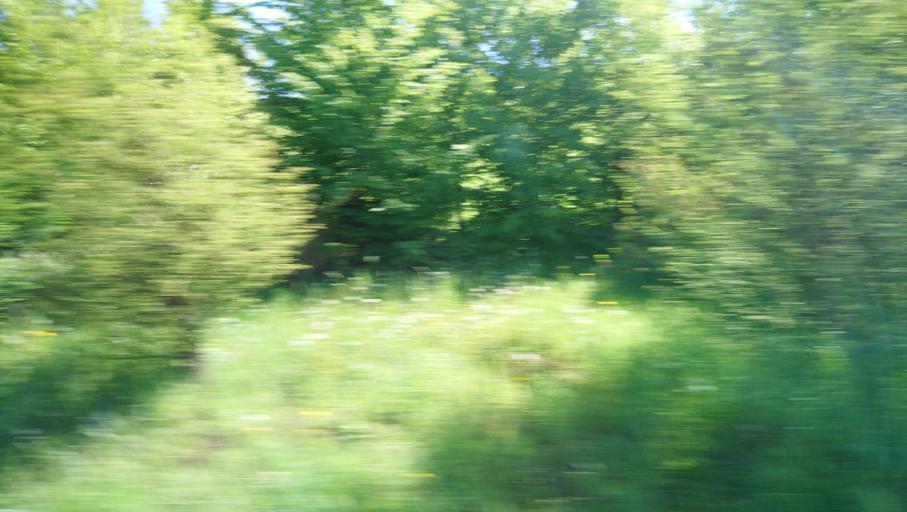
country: LU
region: Diekirch
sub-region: Canton de Vianden
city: Tandel
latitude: 49.8780
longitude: 6.1887
